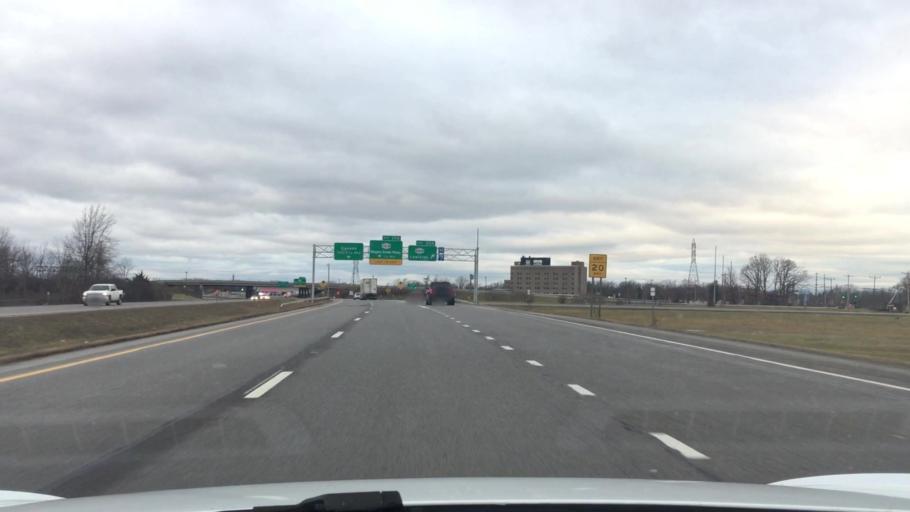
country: US
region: New York
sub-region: Niagara County
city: Lewiston
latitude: 43.1495
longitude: -79.0267
